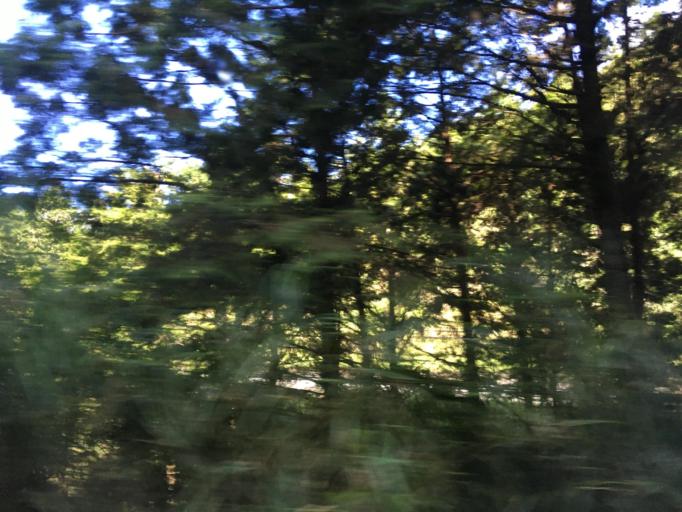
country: TW
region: Taiwan
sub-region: Yilan
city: Yilan
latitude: 24.5137
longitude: 121.5900
